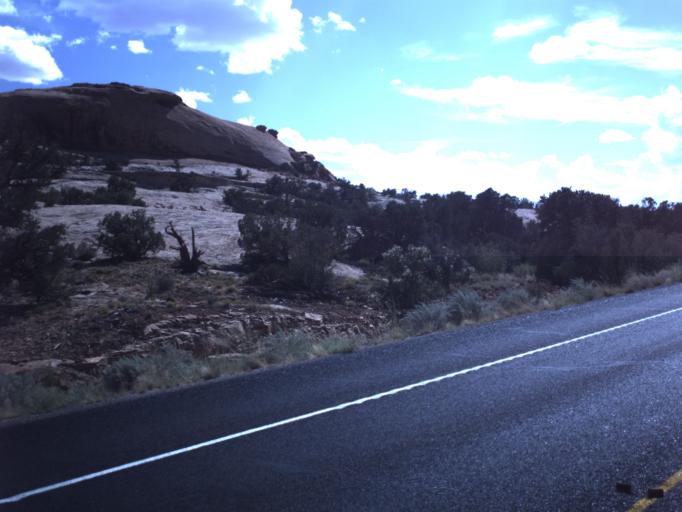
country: US
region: Utah
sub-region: Grand County
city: Moab
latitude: 38.6424
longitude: -109.7406
